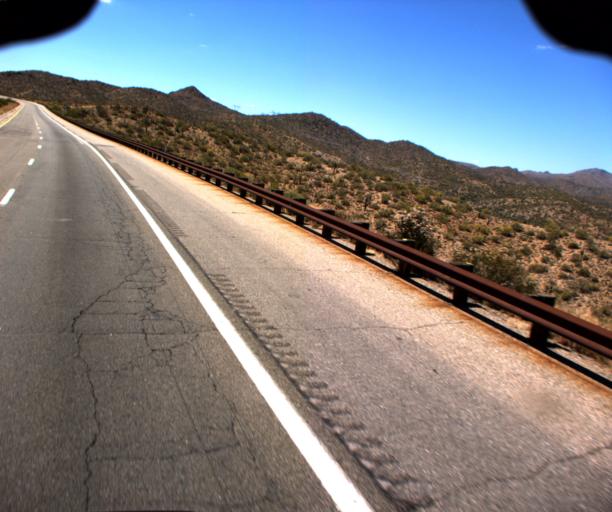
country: US
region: Arizona
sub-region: Yavapai County
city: Bagdad
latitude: 34.4449
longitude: -113.2713
